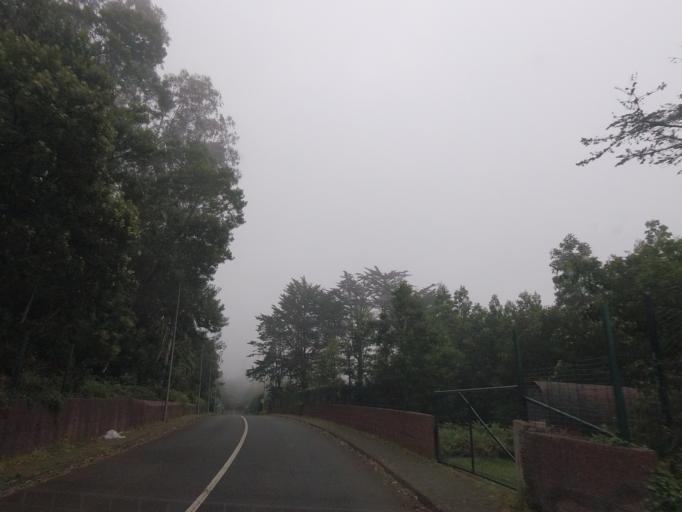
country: PT
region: Madeira
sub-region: Santa Cruz
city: Santa Cruz
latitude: 32.7241
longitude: -16.8259
